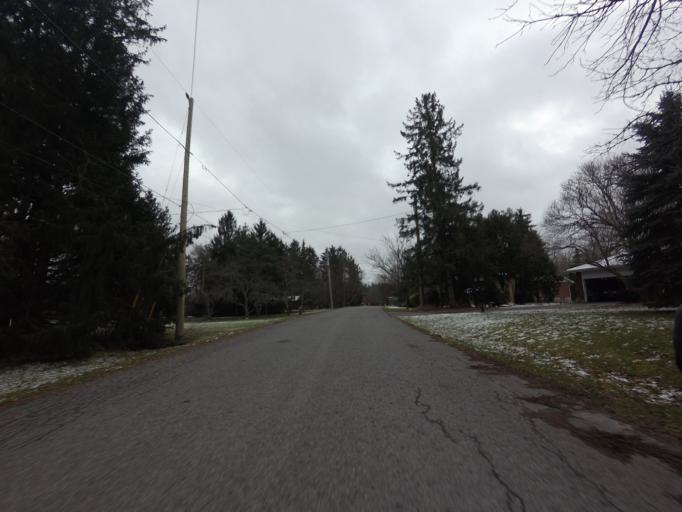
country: CA
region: Ontario
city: Bells Corners
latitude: 45.2459
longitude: -75.7043
